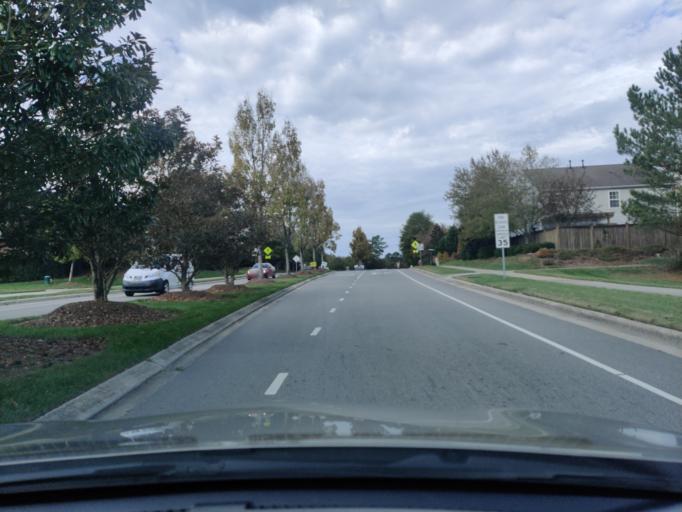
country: US
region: North Carolina
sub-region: Wake County
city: Morrisville
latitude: 35.8404
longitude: -78.8636
